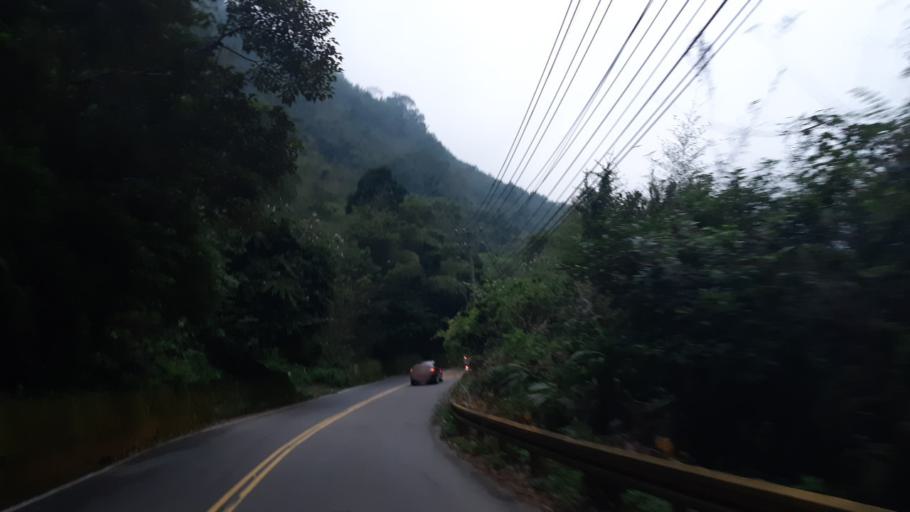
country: TW
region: Taiwan
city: Daxi
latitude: 24.6997
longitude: 121.2168
